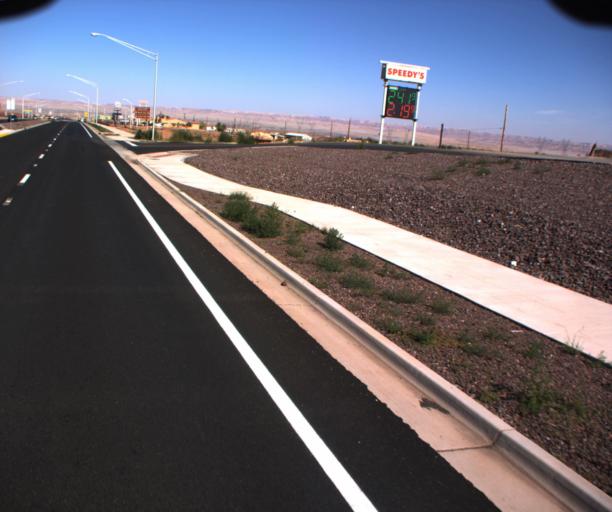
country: US
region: Arizona
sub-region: Coconino County
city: Tuba City
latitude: 35.8508
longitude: -111.4285
